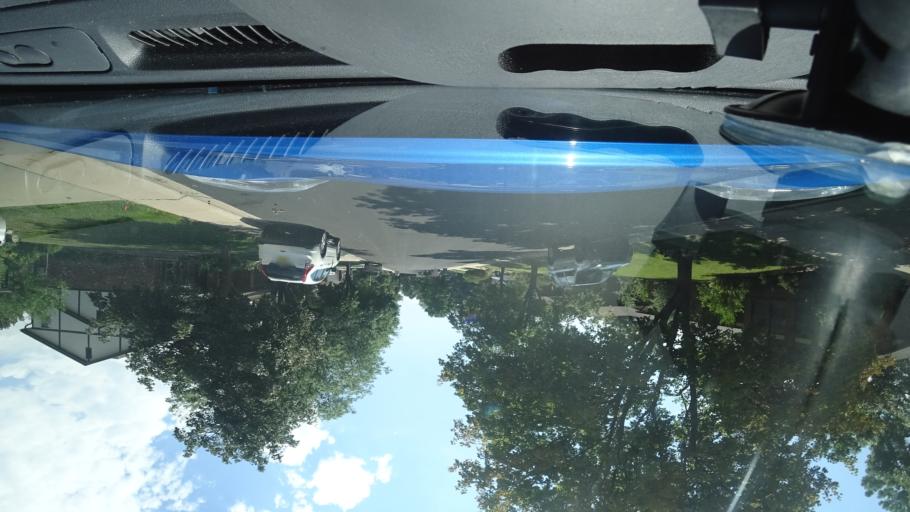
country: US
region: Colorado
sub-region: Adams County
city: Aurora
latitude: 39.7127
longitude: -104.8401
